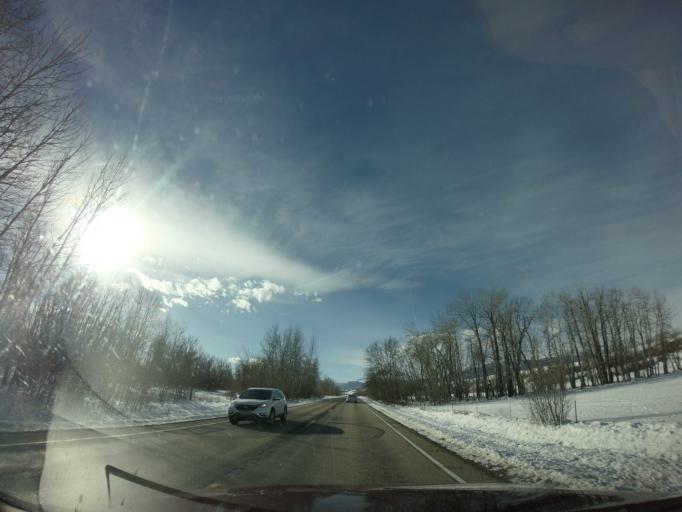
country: US
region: Montana
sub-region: Carbon County
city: Red Lodge
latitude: 45.2539
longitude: -109.2312
